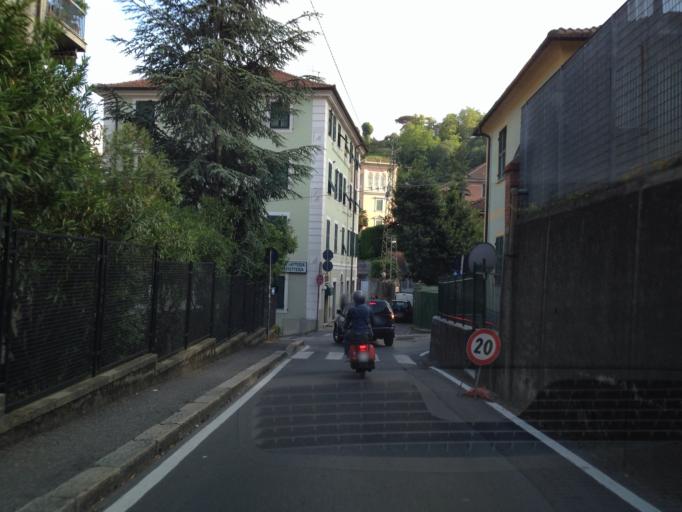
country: IT
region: Liguria
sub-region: Provincia di Genova
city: Santa Marta
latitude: 44.4984
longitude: 8.9005
